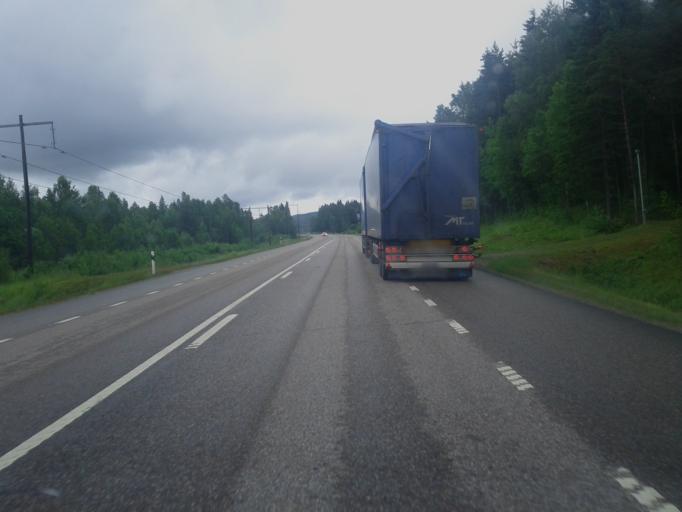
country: SE
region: Vaesternorrland
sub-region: Sundsvalls Kommun
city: Matfors
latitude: 62.3627
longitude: 17.0529
